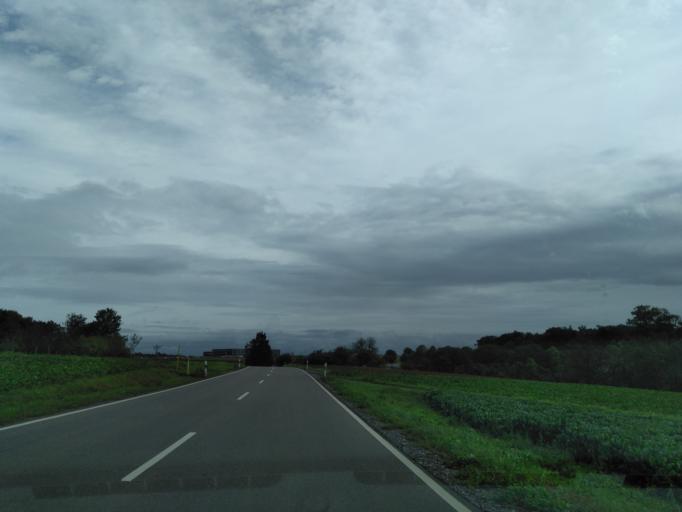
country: DE
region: Baden-Wuerttemberg
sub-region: Regierungsbezirk Stuttgart
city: Oberriexingen
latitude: 48.9439
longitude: 9.0458
